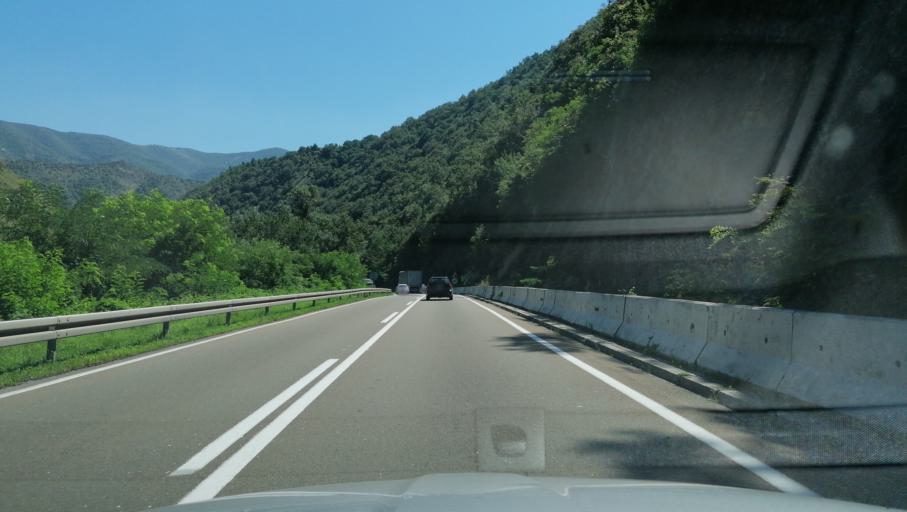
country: RS
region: Central Serbia
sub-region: Raski Okrug
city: Kraljevo
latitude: 43.5632
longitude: 20.6051
